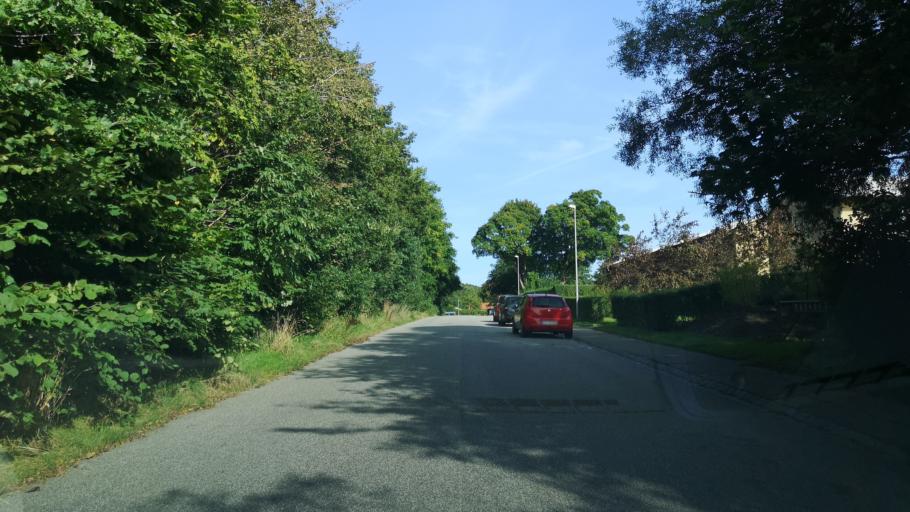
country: DK
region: Central Jutland
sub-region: Herning Kommune
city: Herning
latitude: 56.1660
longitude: 8.9805
